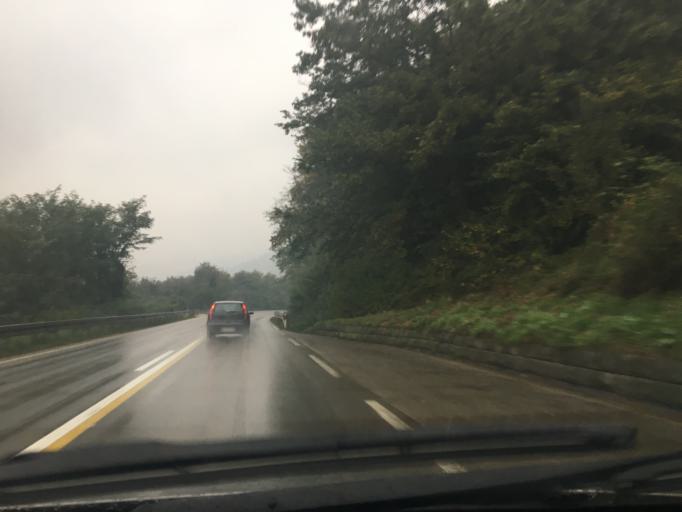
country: RS
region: Central Serbia
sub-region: Pcinjski Okrug
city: Vladicin Han
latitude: 42.8222
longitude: 22.1261
